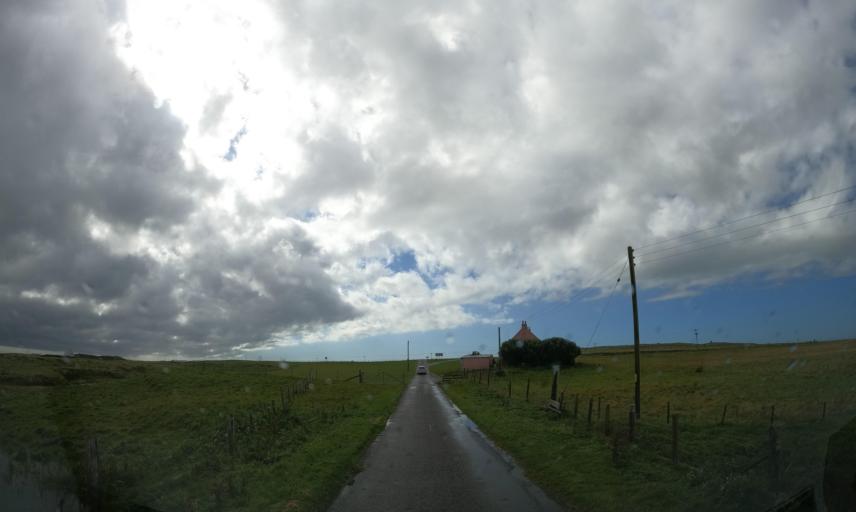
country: GB
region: Scotland
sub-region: Eilean Siar
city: Barra
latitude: 56.5143
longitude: -6.8163
